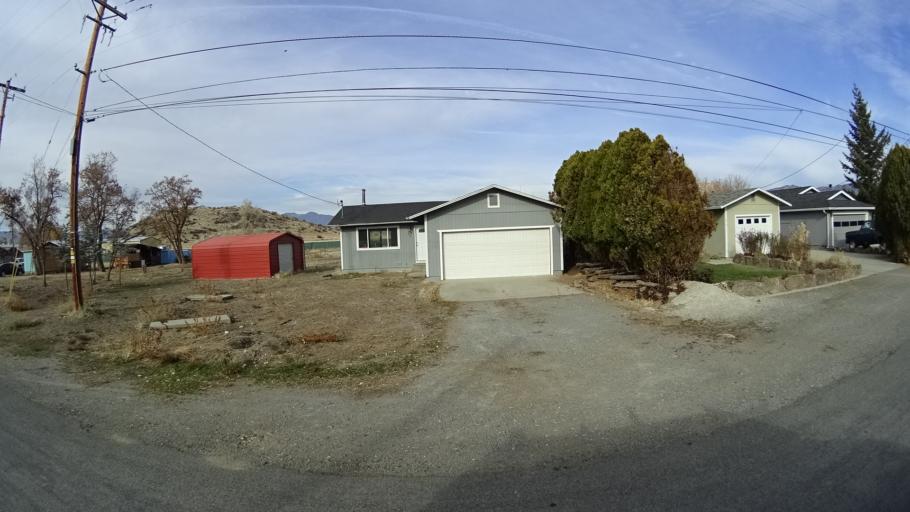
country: US
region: California
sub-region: Siskiyou County
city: Montague
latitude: 41.7287
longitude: -122.5339
